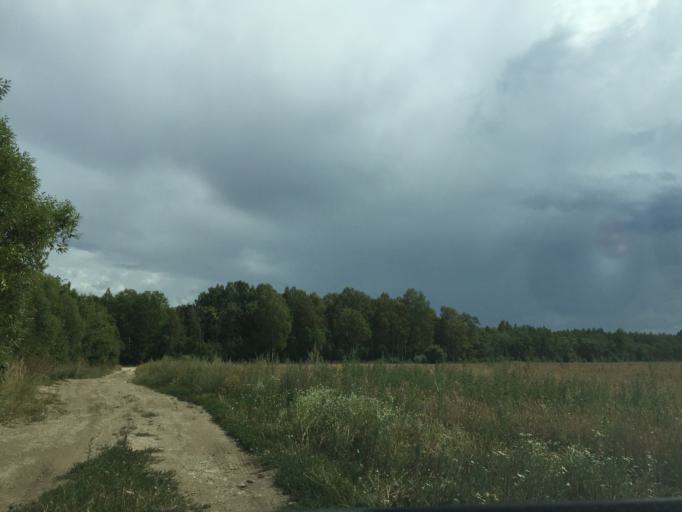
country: LT
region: Siauliu apskritis
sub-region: Joniskis
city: Joniskis
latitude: 56.2978
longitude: 23.6418
